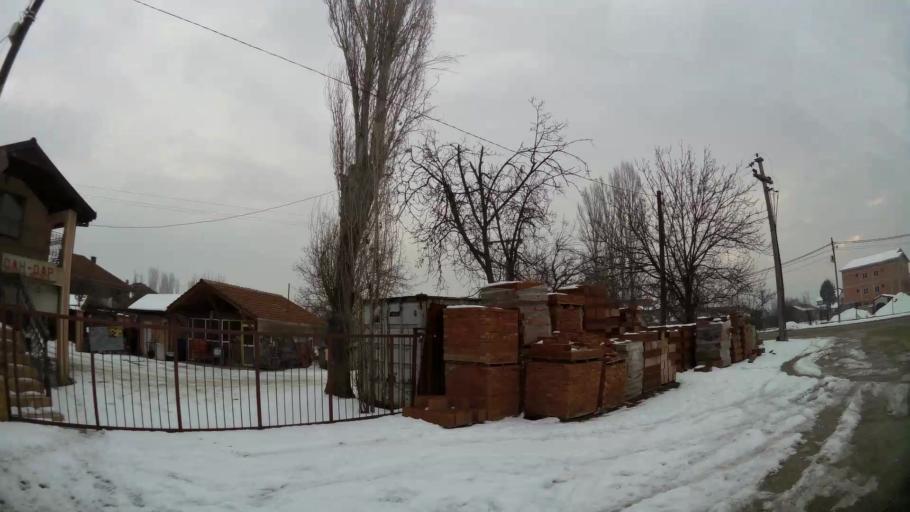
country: MK
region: Saraj
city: Saraj
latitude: 42.0450
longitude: 21.3576
